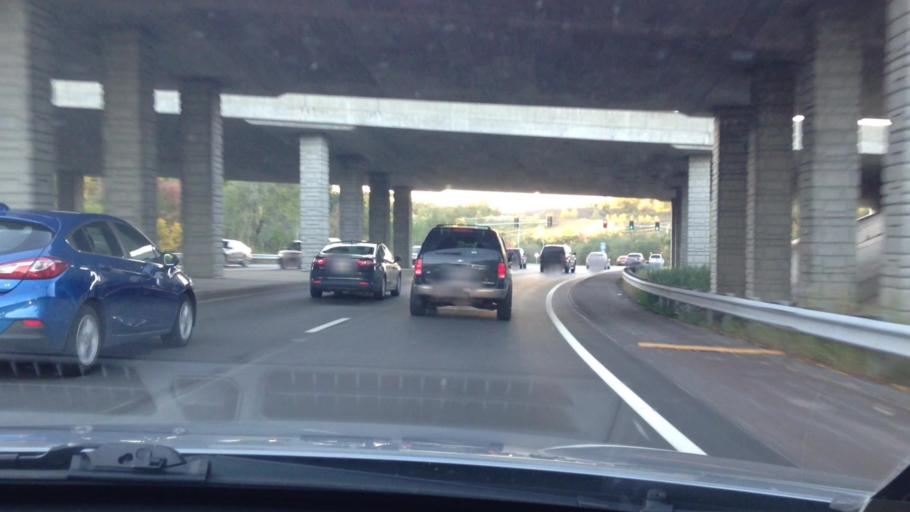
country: US
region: Missouri
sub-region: Jackson County
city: Raytown
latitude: 39.0113
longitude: -94.4979
